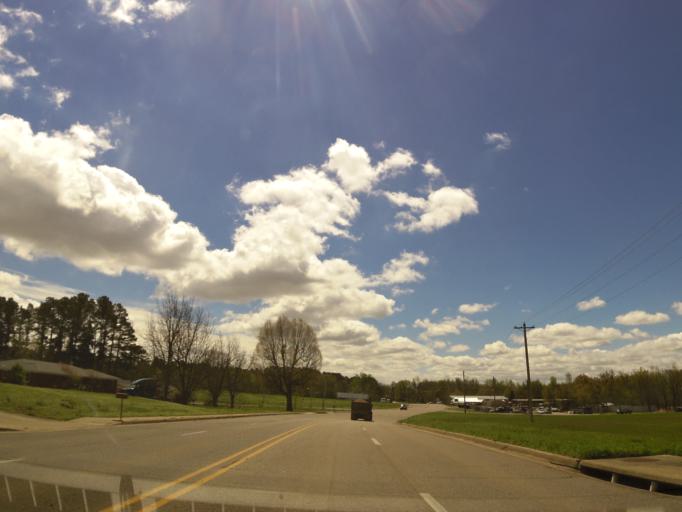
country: US
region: Arkansas
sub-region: Craighead County
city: Jonesboro
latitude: 35.8805
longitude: -90.7021
